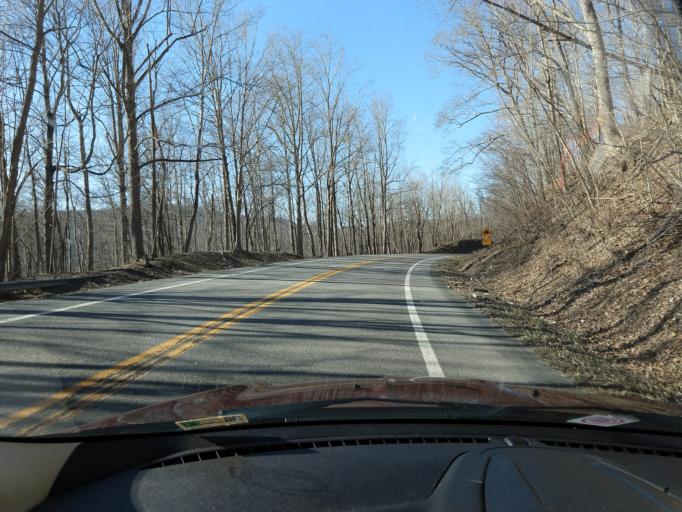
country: US
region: West Virginia
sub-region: Summers County
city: Hinton
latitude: 37.7538
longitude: -80.8983
